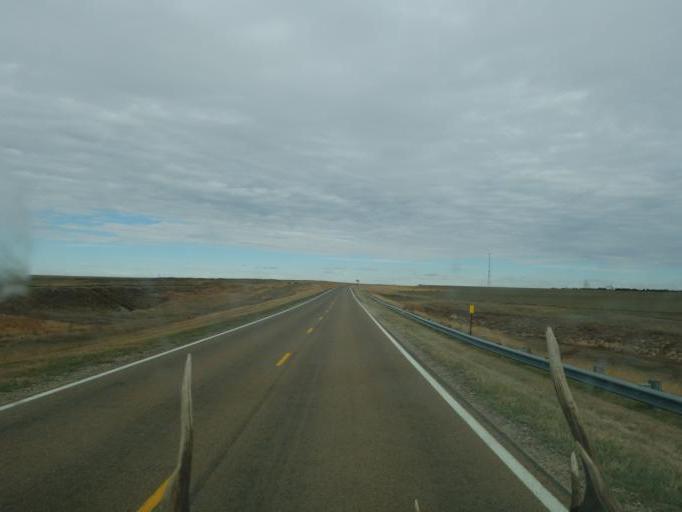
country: US
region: Kansas
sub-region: Thomas County
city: Colby
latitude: 39.0431
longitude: -101.2704
